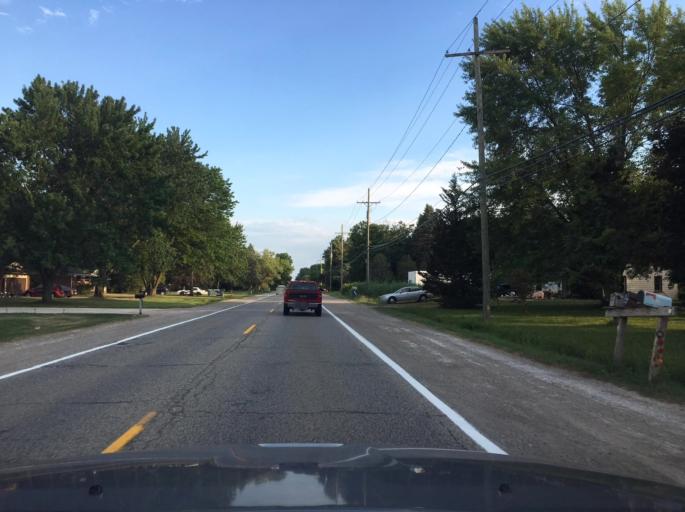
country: US
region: Michigan
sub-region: Macomb County
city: Mount Clemens
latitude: 42.6685
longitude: -82.8777
